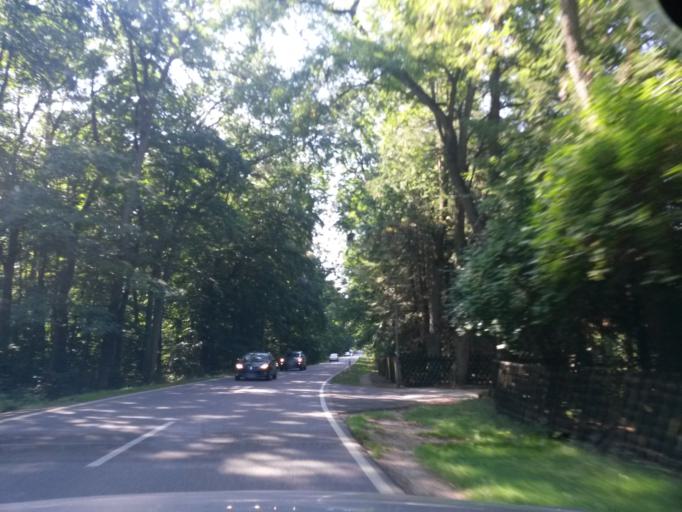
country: DE
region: Brandenburg
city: Marienwerder
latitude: 52.8982
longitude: 13.6413
